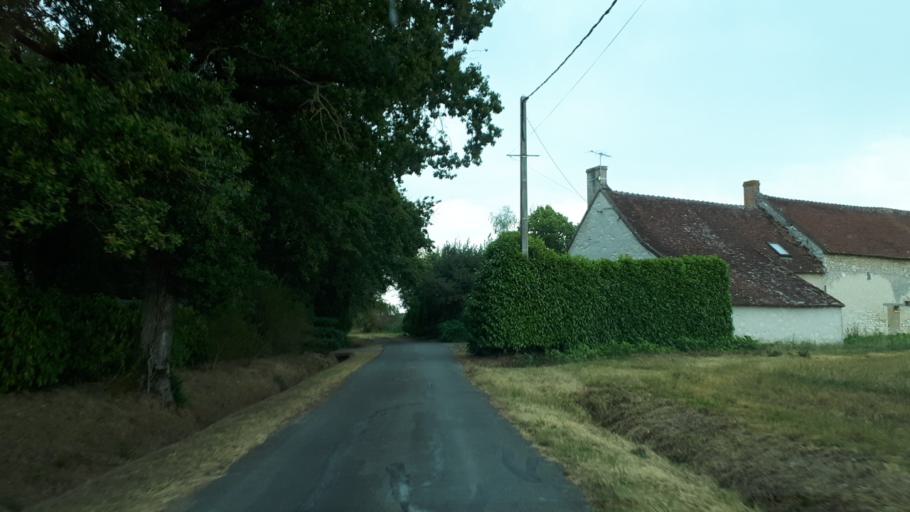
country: FR
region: Centre
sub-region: Departement du Loir-et-Cher
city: Saint-Romain-sur-Cher
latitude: 47.3549
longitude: 1.3933
